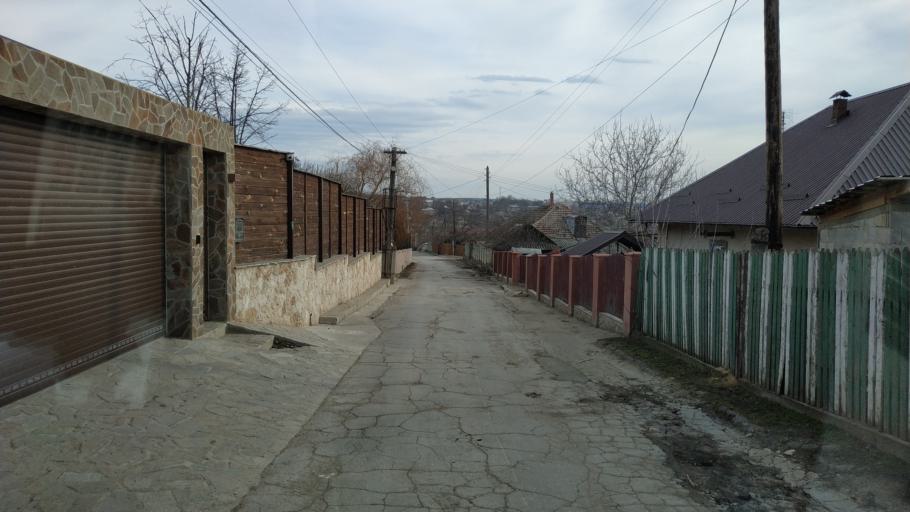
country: MD
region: Chisinau
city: Vatra
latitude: 46.9818
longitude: 28.6644
